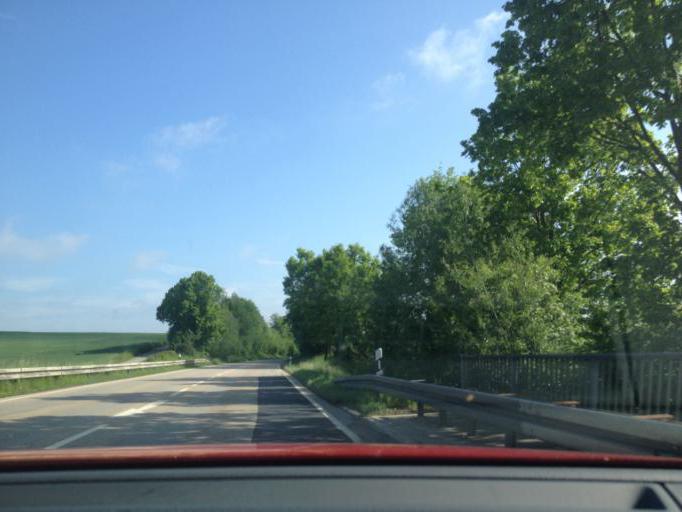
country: DE
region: Bavaria
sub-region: Upper Palatinate
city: Kemnath
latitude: 49.8704
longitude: 11.8760
